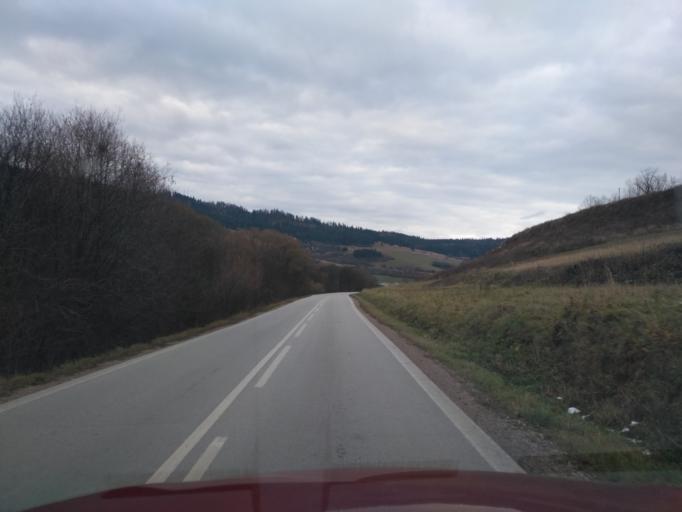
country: SK
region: Kosicky
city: Spisska Nova Ves
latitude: 48.8381
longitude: 20.6377
